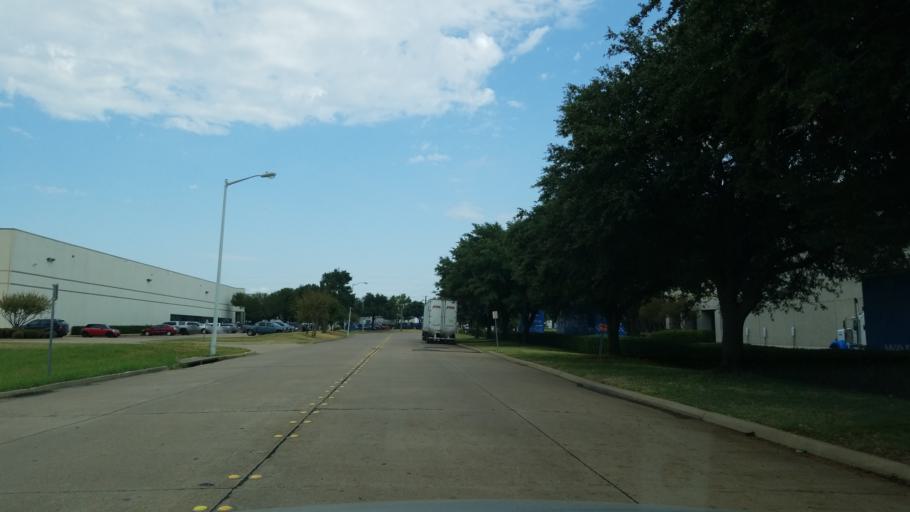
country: US
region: Texas
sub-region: Dallas County
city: Garland
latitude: 32.9047
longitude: -96.6741
